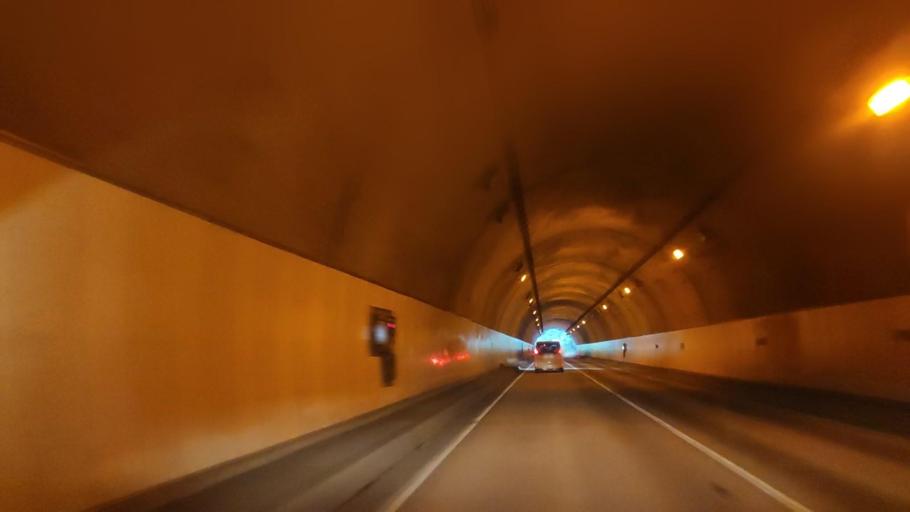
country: JP
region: Hokkaido
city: Shimo-furano
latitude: 43.3409
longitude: 142.2730
